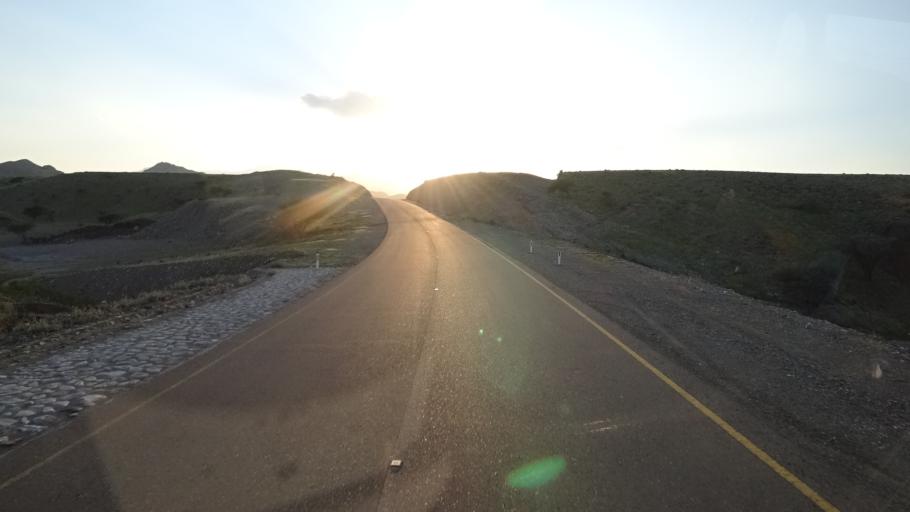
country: OM
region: Al Batinah
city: Al Khaburah
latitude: 23.7892
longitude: 56.9458
